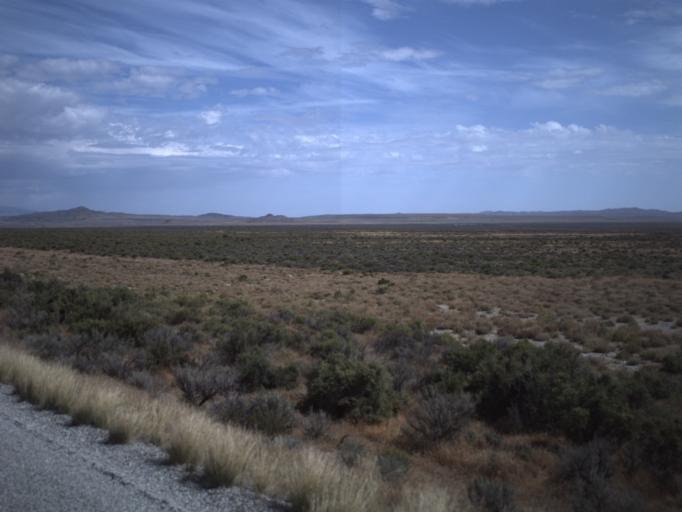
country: US
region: Utah
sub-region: Tooele County
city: Wendover
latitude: 41.5544
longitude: -113.5854
